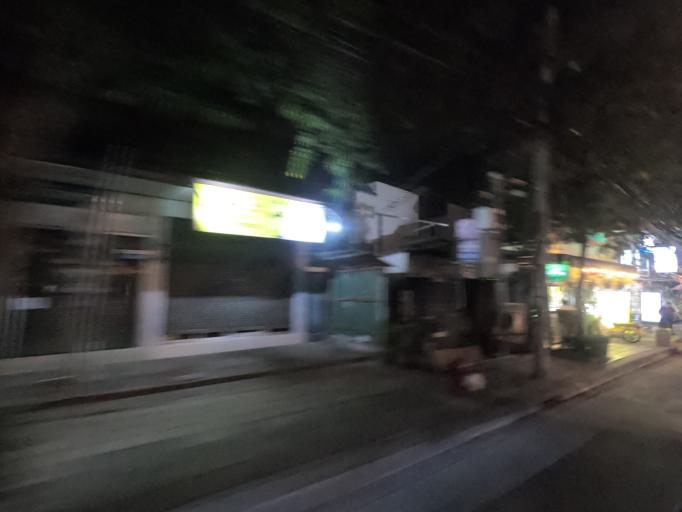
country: TH
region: Bangkok
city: Lat Phrao
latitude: 13.8007
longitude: 100.6067
